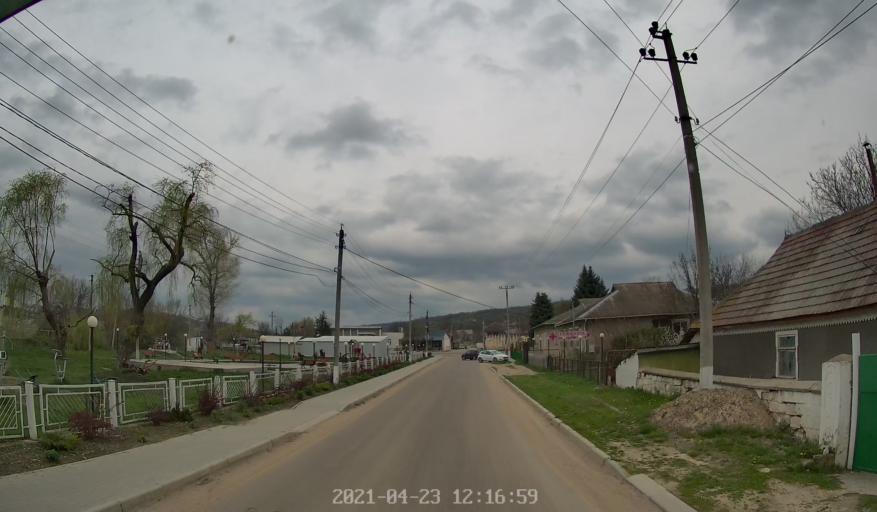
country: MD
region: Chisinau
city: Vadul lui Voda
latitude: 47.1230
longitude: 29.0018
